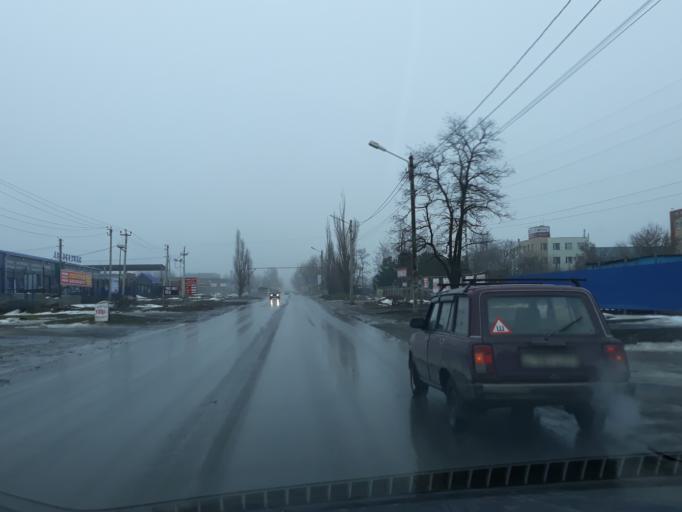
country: RU
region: Rostov
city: Novobessergenovka
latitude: 47.2111
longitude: 38.8674
